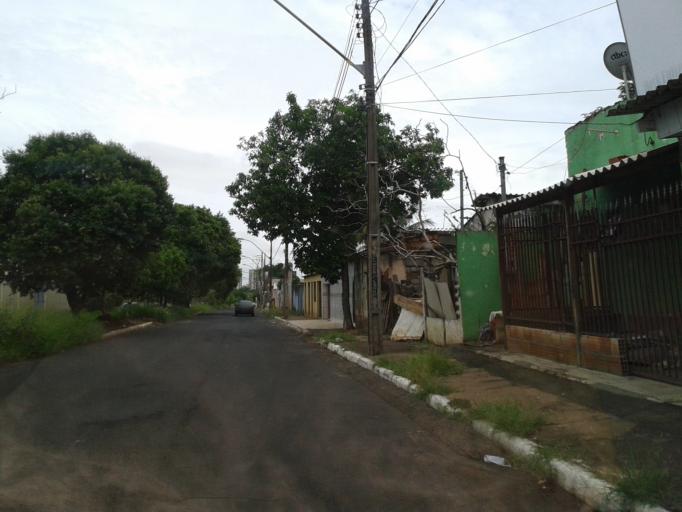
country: BR
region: Minas Gerais
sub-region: Uberlandia
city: Uberlandia
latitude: -18.9360
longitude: -48.2424
